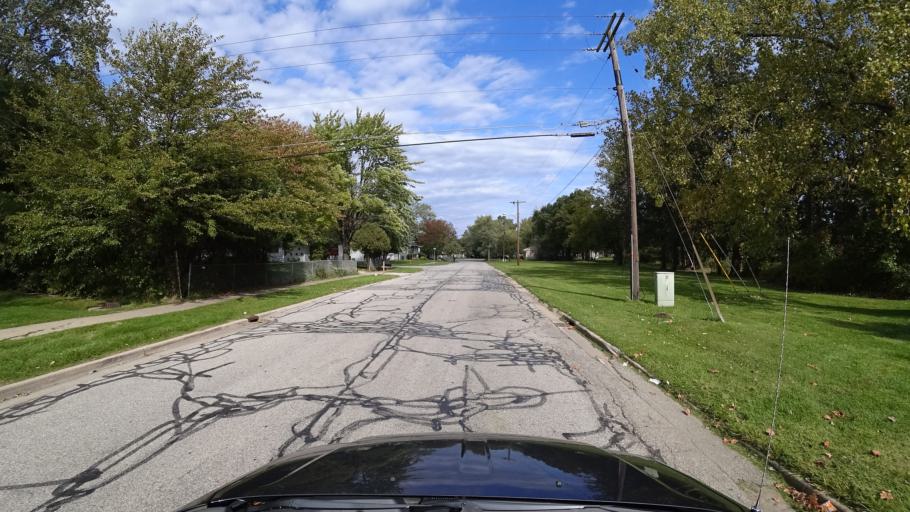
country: US
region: Indiana
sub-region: LaPorte County
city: Michigan City
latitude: 41.6704
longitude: -86.9005
